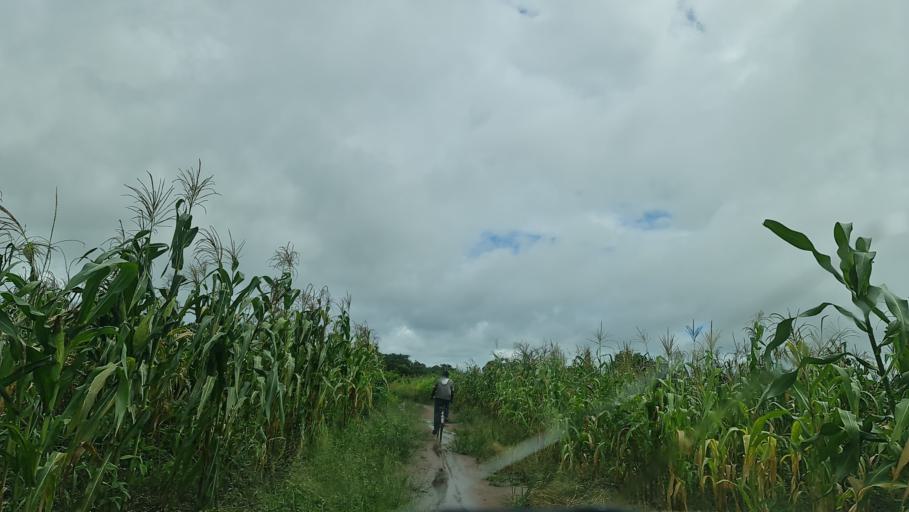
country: MW
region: Southern Region
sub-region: Nsanje District
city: Nsanje
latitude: -17.4443
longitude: 35.8451
